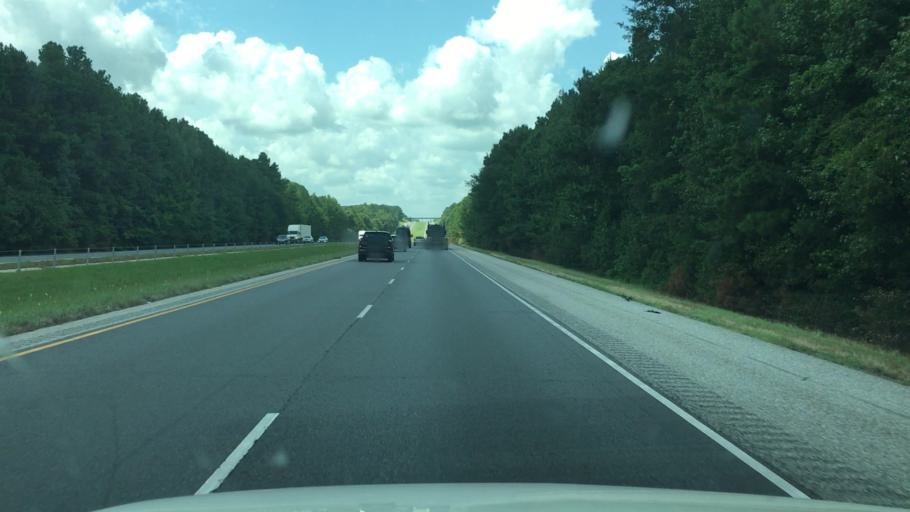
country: US
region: Arkansas
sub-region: Clark County
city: Arkadelphia
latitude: 34.0854
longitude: -93.1127
